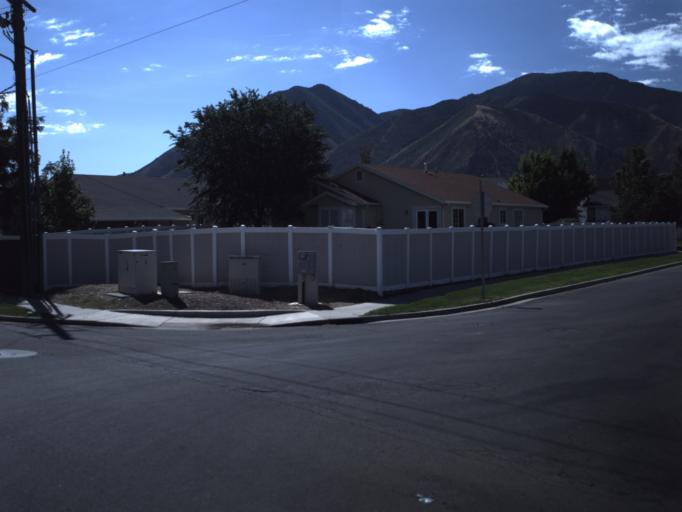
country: US
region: Utah
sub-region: Utah County
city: Spanish Fork
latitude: 40.1001
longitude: -111.6310
